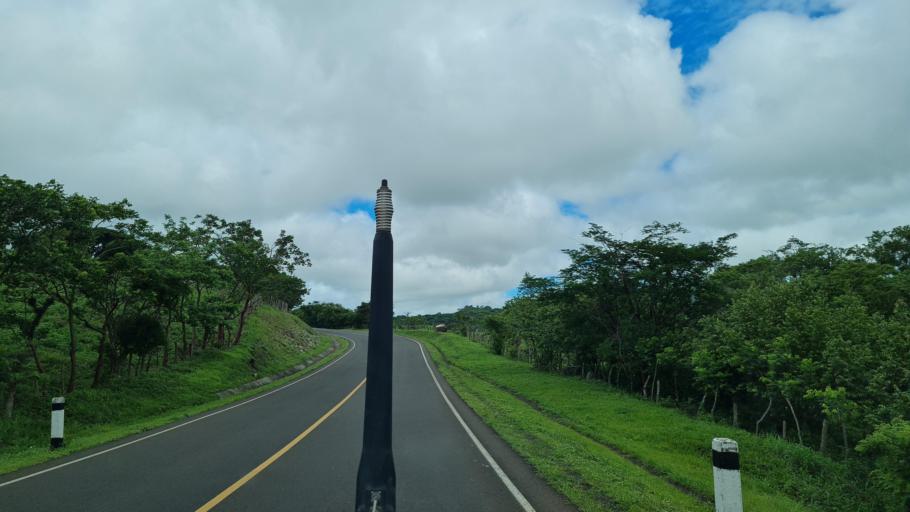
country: NI
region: Matagalpa
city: Terrabona
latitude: 12.5968
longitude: -85.9310
